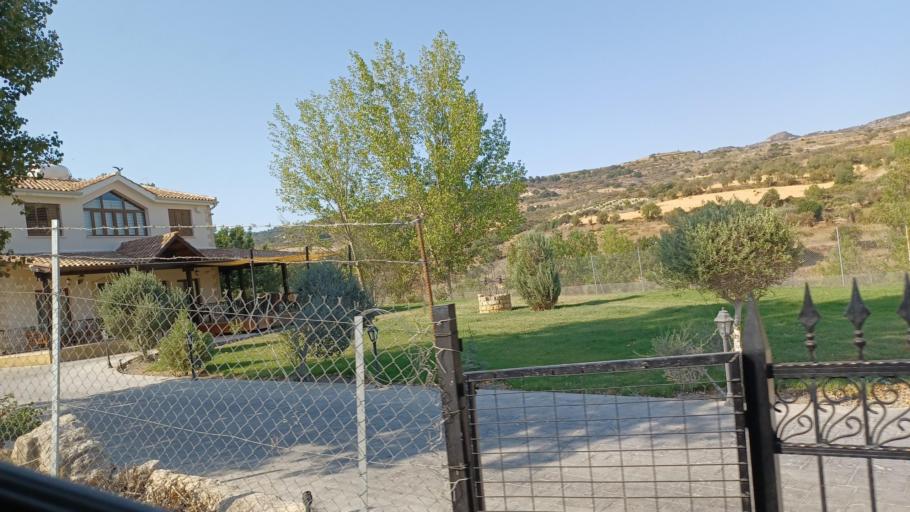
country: CY
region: Pafos
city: Tala
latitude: 34.9140
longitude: 32.4793
